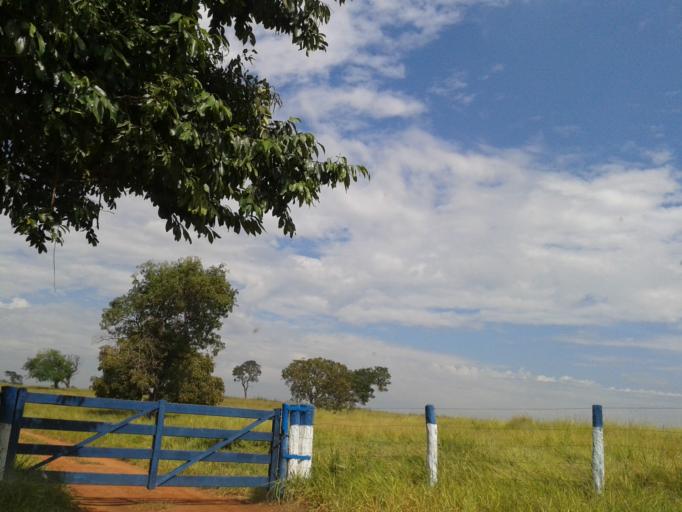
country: BR
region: Minas Gerais
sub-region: Campina Verde
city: Campina Verde
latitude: -19.3929
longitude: -49.6375
